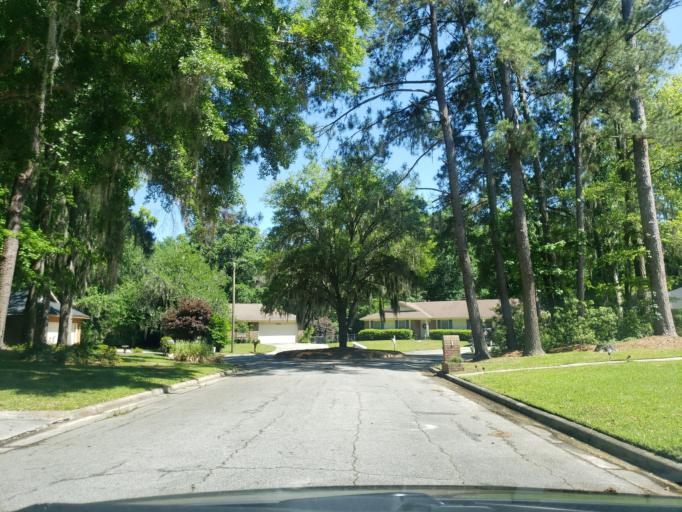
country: US
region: Georgia
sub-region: Chatham County
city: Isle of Hope
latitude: 31.9880
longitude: -81.0915
